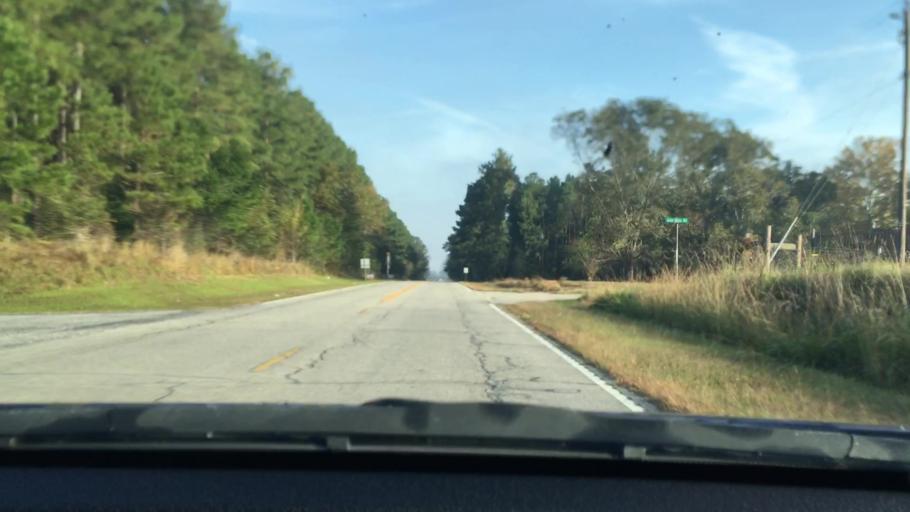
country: US
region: South Carolina
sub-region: Sumter County
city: East Sumter
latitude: 33.9734
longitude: -80.2996
